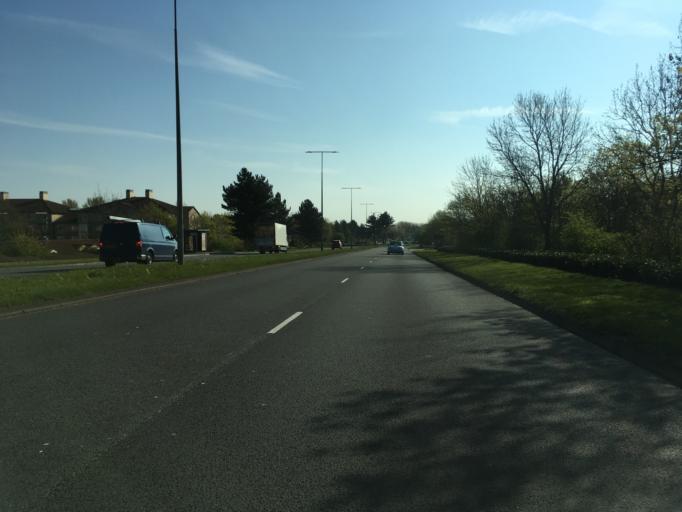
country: GB
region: England
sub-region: Milton Keynes
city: Milton Keynes
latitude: 52.0540
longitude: -0.7312
